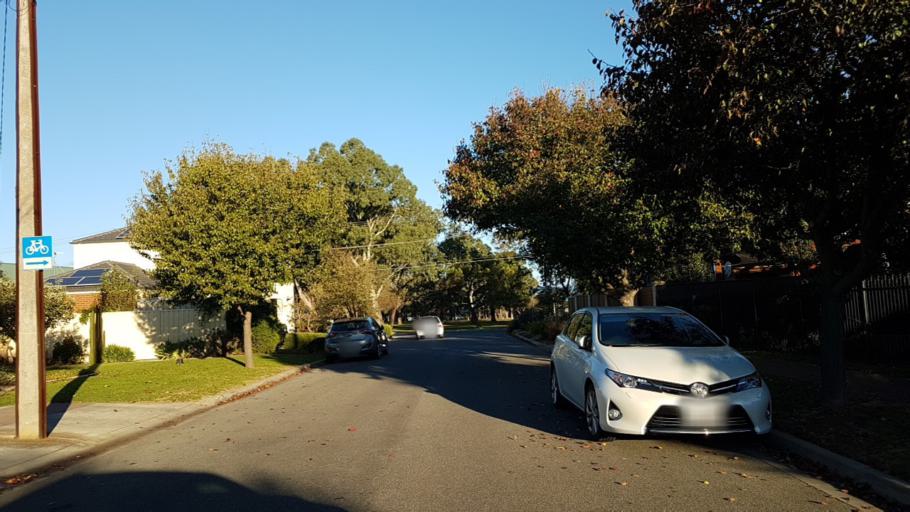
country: AU
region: South Australia
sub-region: Charles Sturt
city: Henley Beach
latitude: -34.9279
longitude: 138.5034
